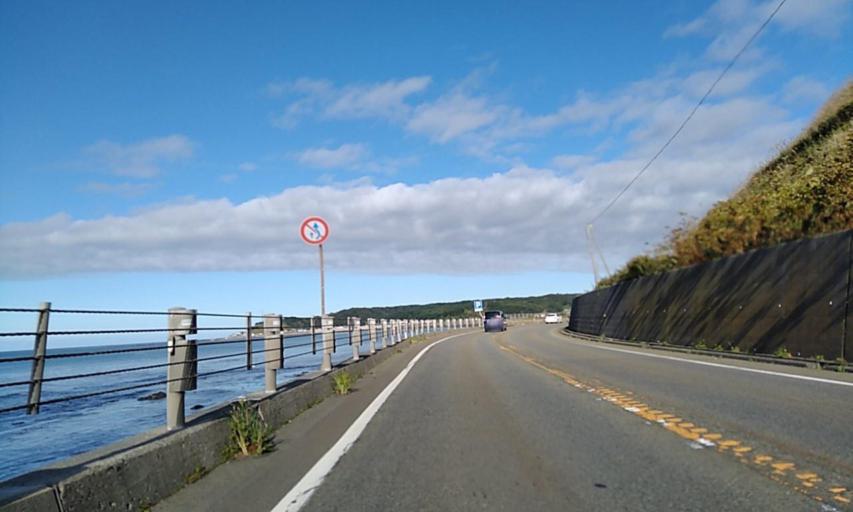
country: JP
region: Hokkaido
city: Shizunai-furukawacho
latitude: 42.2633
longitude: 142.5162
